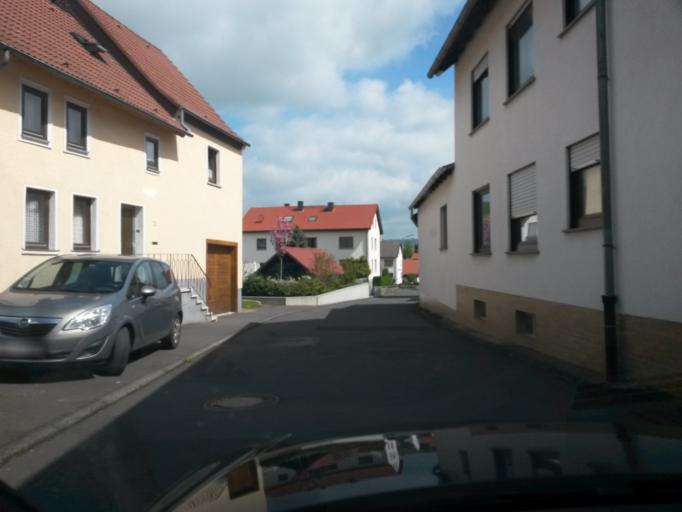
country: DE
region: Thuringia
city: Birx
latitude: 50.5000
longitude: 10.0020
